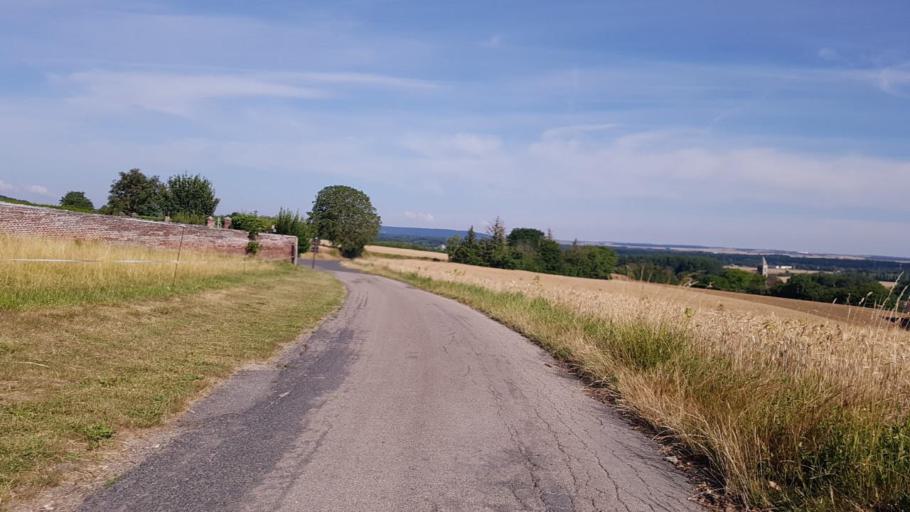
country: FR
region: Picardie
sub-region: Departement de l'Oise
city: Pontpoint
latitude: 49.2962
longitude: 2.6429
